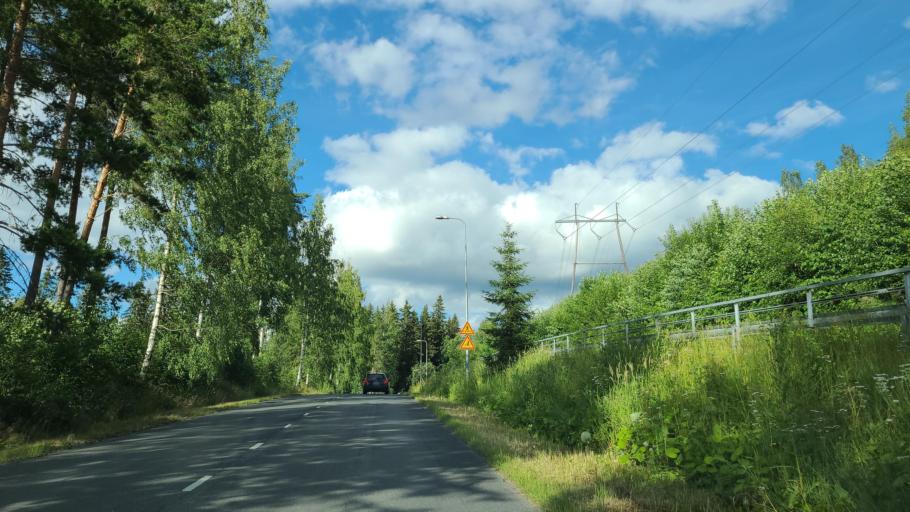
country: FI
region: Northern Savo
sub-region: Kuopio
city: Kuopio
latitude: 62.9375
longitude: 27.6371
